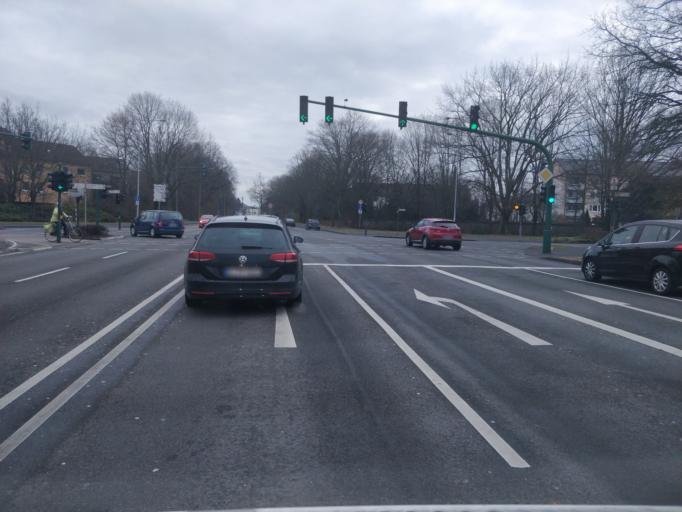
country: DE
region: North Rhine-Westphalia
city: Opladen
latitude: 51.0259
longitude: 7.0363
